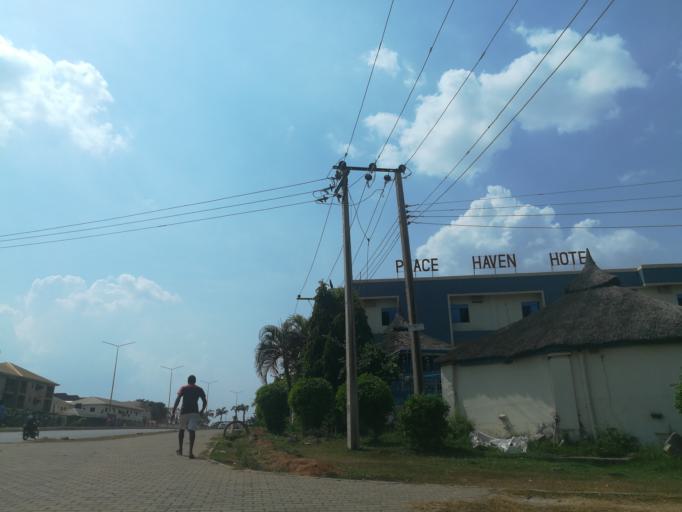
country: NG
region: Abuja Federal Capital Territory
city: Abuja
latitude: 9.0531
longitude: 7.4490
